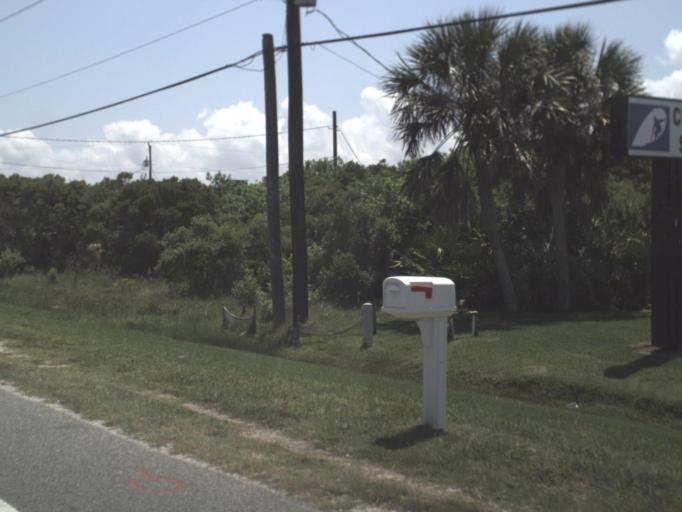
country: US
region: Florida
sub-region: Saint Johns County
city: Butler Beach
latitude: 29.7743
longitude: -81.2560
